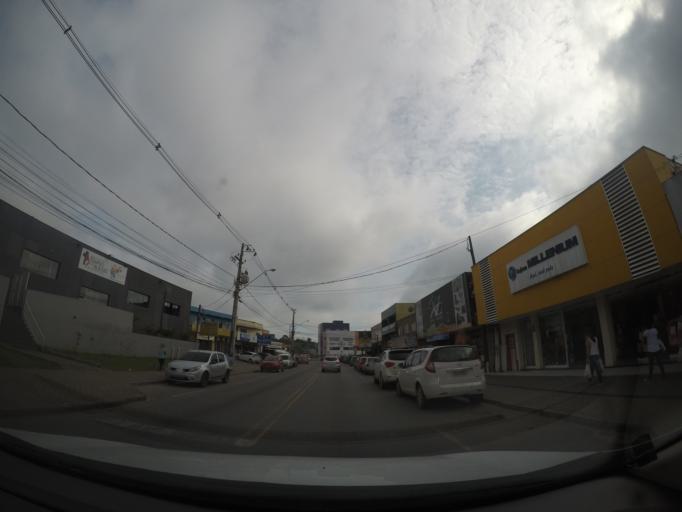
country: BR
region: Parana
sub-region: Colombo
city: Colombo
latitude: -25.3511
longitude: -49.2008
